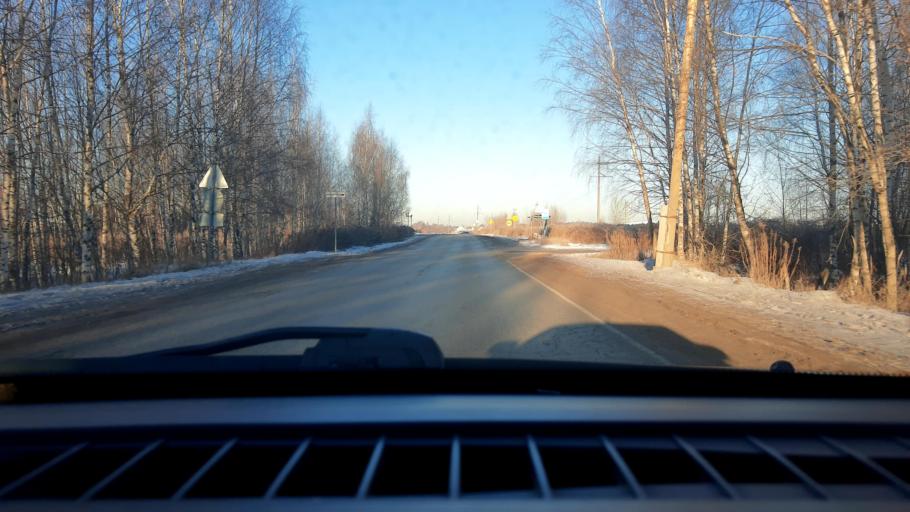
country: RU
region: Nizjnij Novgorod
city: Bor
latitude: 56.3930
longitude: 44.0386
